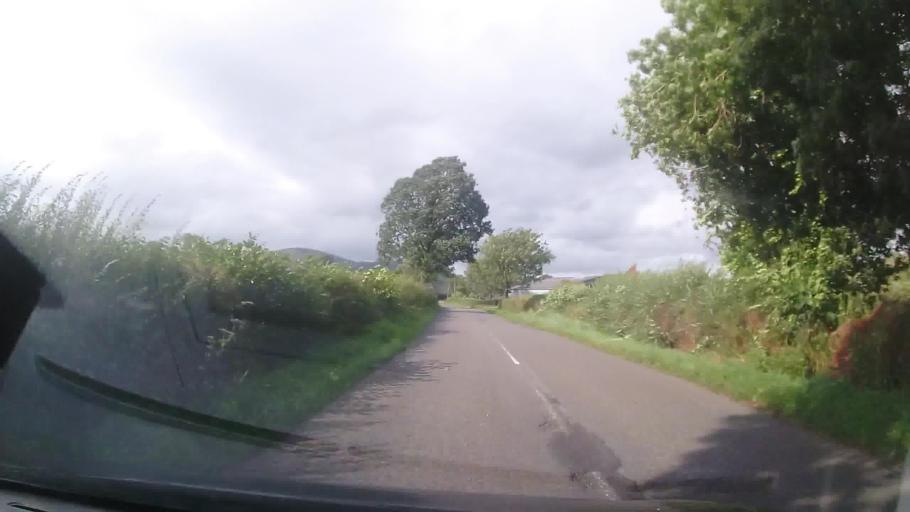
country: GB
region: England
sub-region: Shropshire
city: Lydham
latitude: 52.5128
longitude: -2.9650
